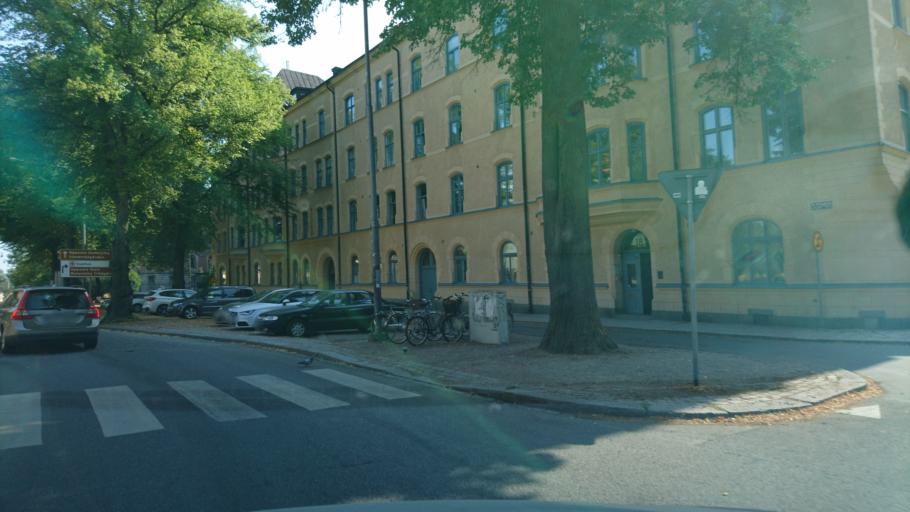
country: SE
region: Uppsala
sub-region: Uppsala Kommun
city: Uppsala
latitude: 59.8570
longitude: 17.6267
